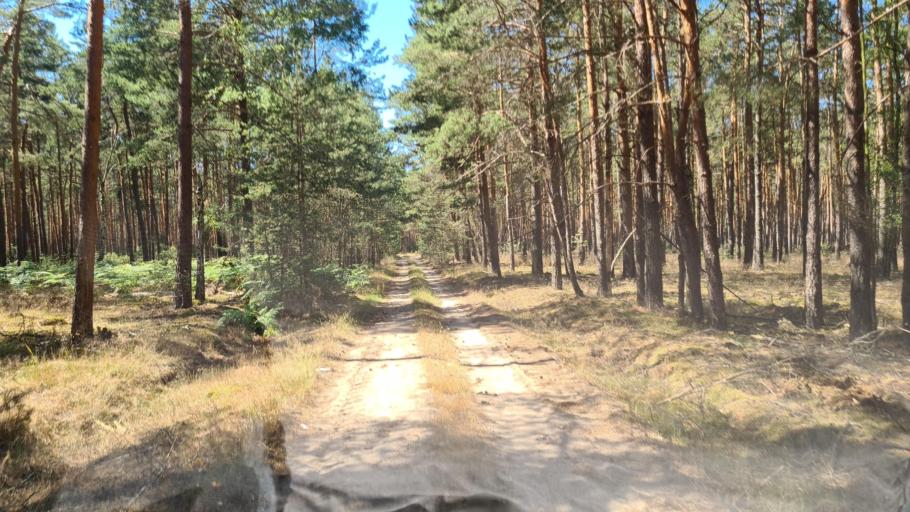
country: DE
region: Brandenburg
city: Treuenbrietzen
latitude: 52.0558
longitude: 12.7974
